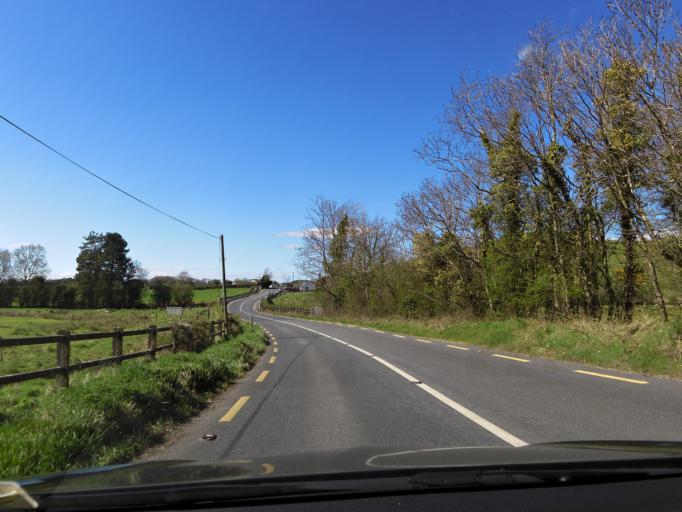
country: IE
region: Leinster
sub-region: Kildare
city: Moone
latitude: 52.9881
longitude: -6.7866
